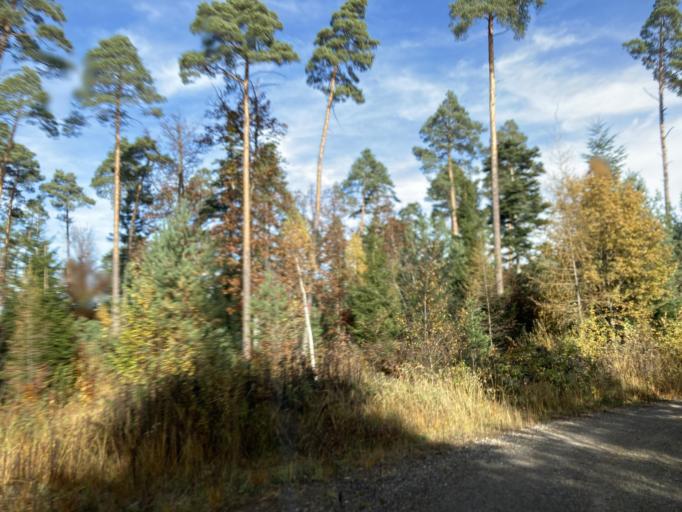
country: DE
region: Baden-Wuerttemberg
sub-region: Tuebingen Region
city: Bodelshausen
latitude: 48.4183
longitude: 8.9624
